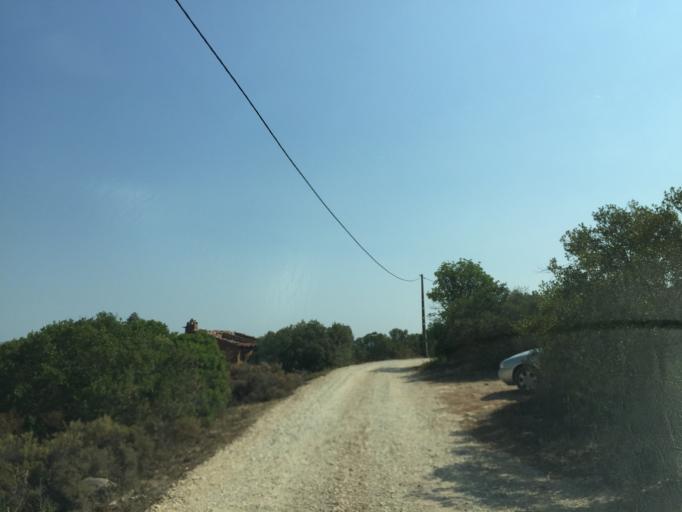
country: PT
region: Faro
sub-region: Faro
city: Santa Barbara de Nexe
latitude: 37.1146
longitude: -7.9931
